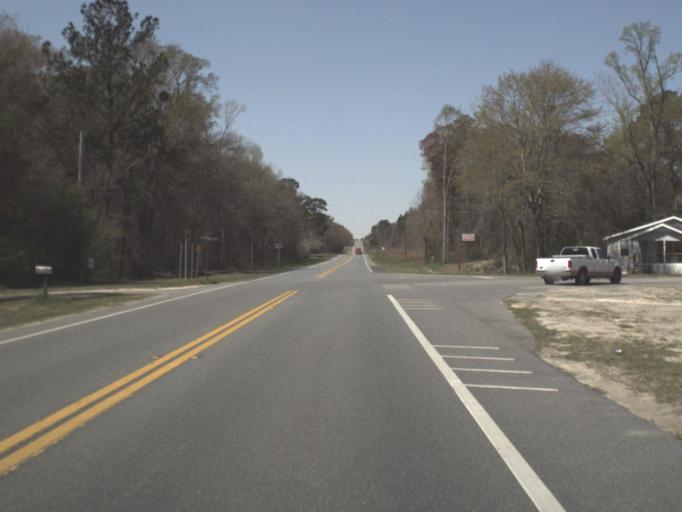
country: US
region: Florida
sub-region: Jackson County
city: Graceville
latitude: 30.9727
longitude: -85.6173
